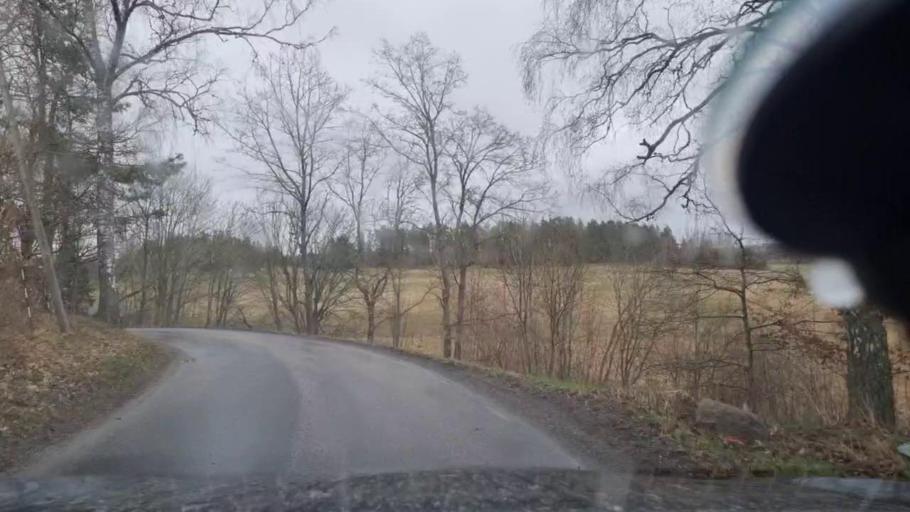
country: SE
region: Stockholm
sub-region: Vallentuna Kommun
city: Vallentuna
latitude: 59.5259
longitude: 18.0396
